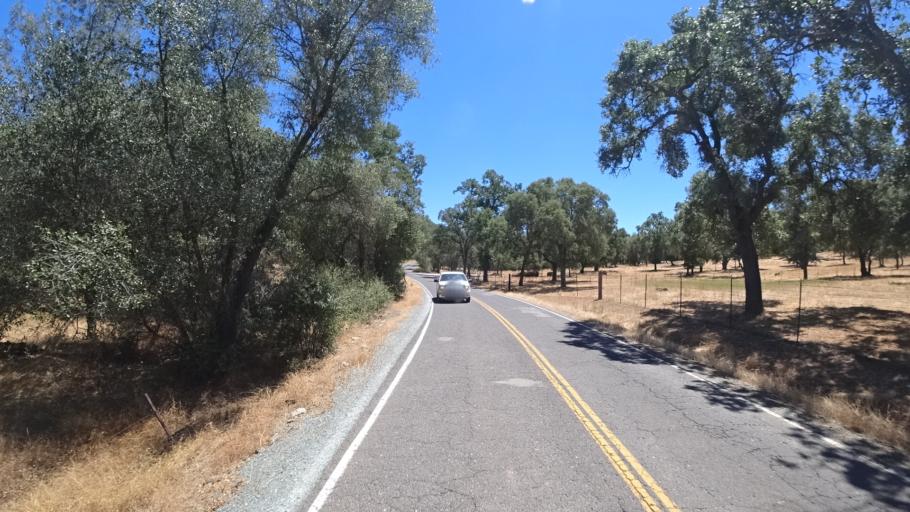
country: US
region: California
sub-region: Calaveras County
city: Copperopolis
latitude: 38.0602
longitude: -120.6534
